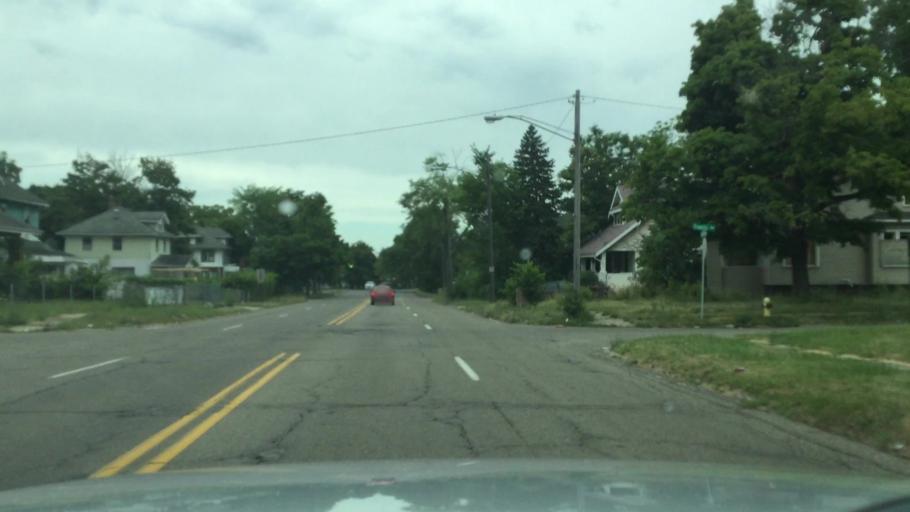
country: US
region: Michigan
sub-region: Genesee County
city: Flint
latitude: 43.0362
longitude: -83.7021
